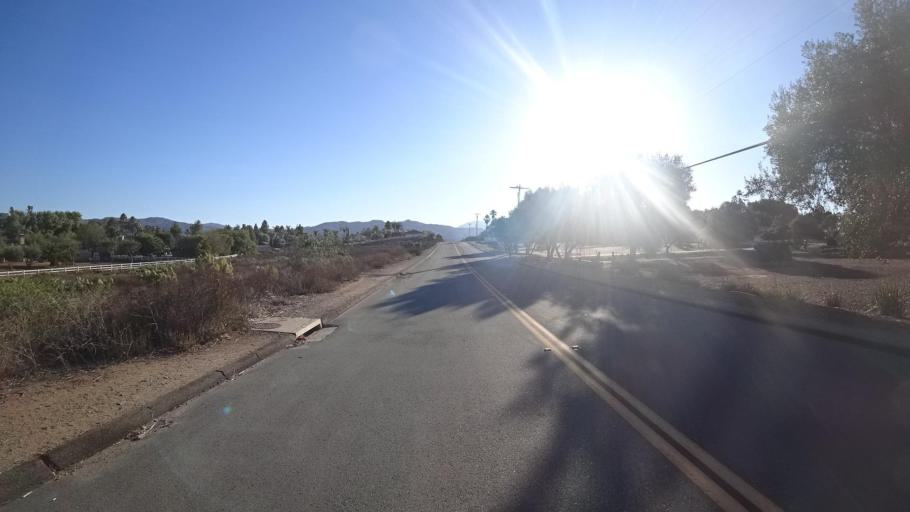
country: US
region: California
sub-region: San Diego County
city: Jamul
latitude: 32.7066
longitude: -116.8804
